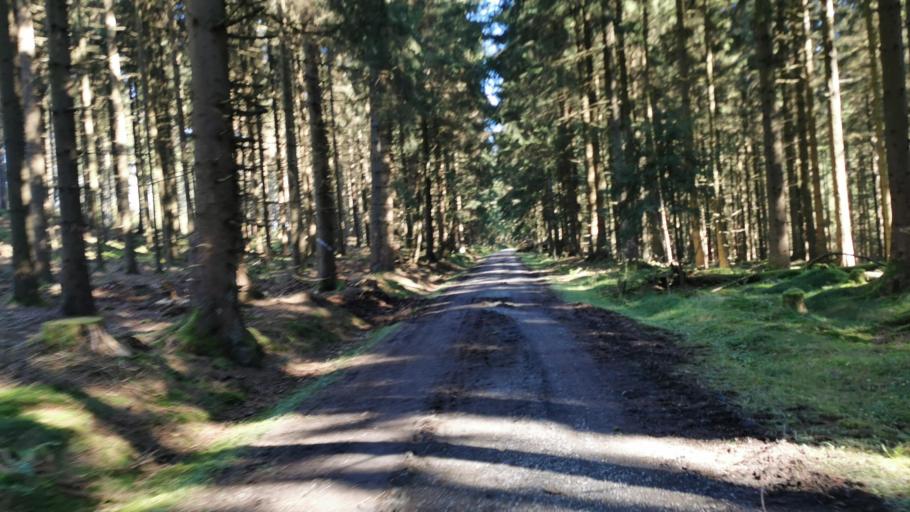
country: DE
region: Bavaria
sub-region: Upper Franconia
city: Tettau
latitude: 50.4743
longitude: 11.2715
